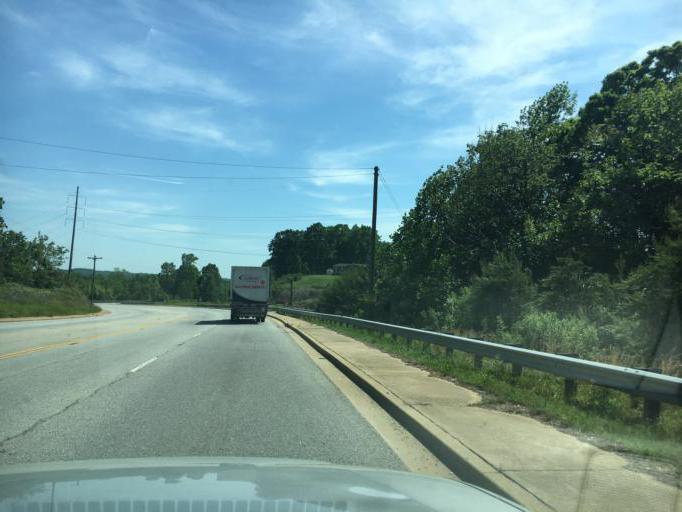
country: US
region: South Carolina
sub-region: Cherokee County
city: Blacksburg
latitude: 35.1345
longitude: -81.5099
